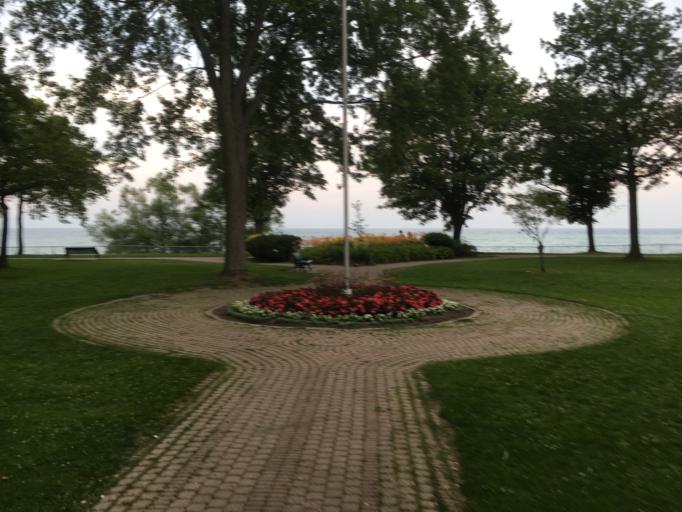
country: CA
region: Ontario
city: Oshawa
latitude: 43.8624
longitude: -78.8289
